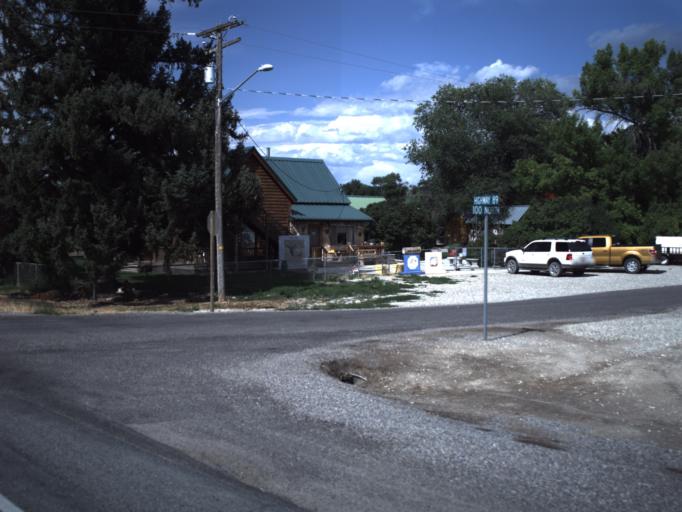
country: US
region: Utah
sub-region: Sanpete County
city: Manti
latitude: 39.1947
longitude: -111.6925
